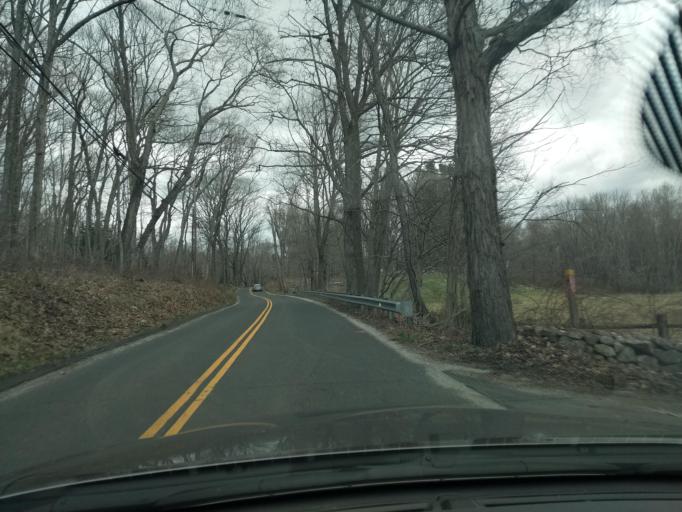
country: US
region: Connecticut
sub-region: Fairfield County
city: Newtown
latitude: 41.3709
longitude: -73.2828
